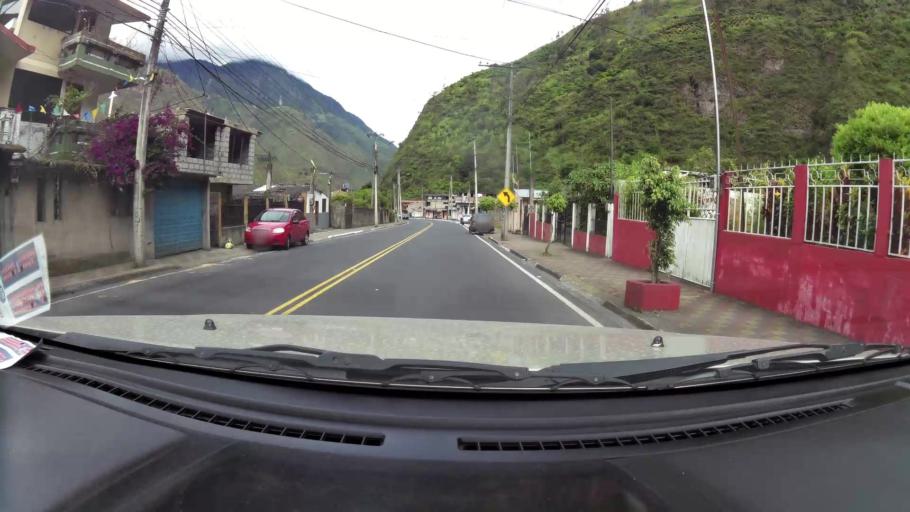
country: EC
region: Tungurahua
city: Banos
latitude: -1.3955
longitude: -78.4051
